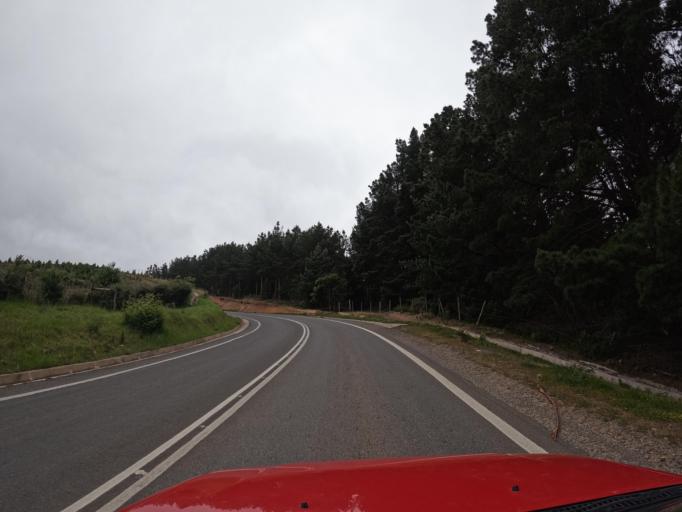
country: CL
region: O'Higgins
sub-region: Provincia de Colchagua
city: Santa Cruz
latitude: -34.6295
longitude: -72.0162
